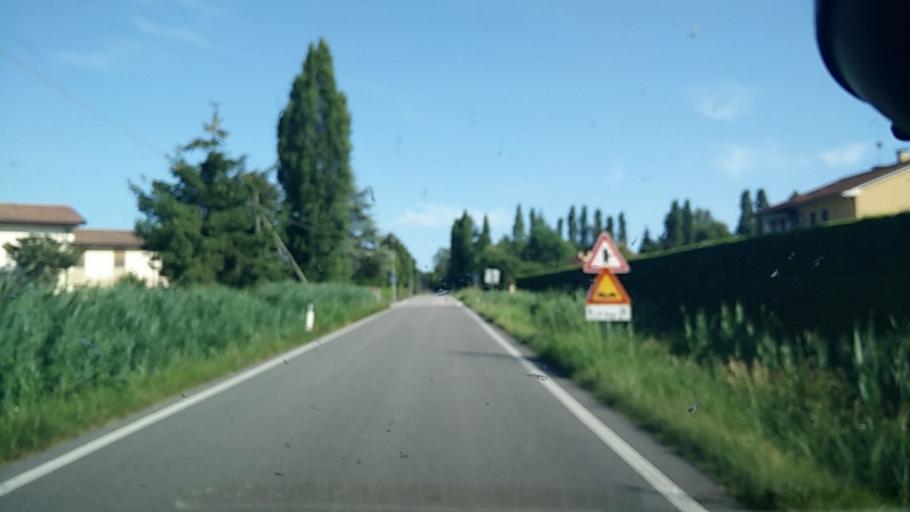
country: IT
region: Veneto
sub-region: Provincia di Treviso
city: San Biagio di Callalta
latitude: 45.6812
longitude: 12.3994
